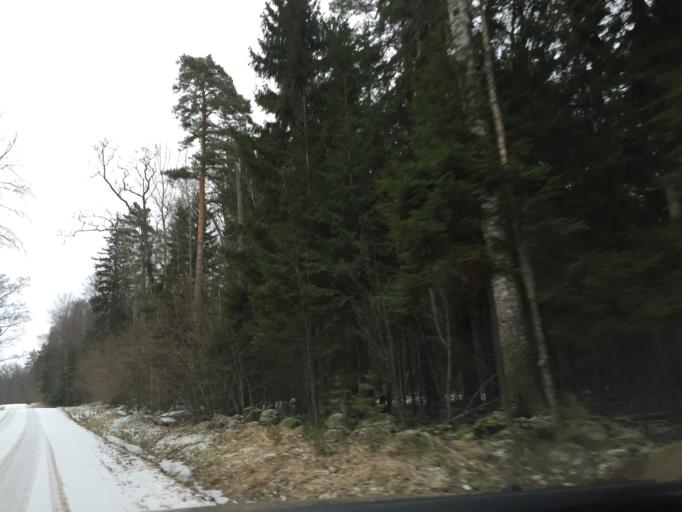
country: LV
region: Salacgrivas
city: Salacgriva
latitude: 57.5173
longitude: 24.3830
